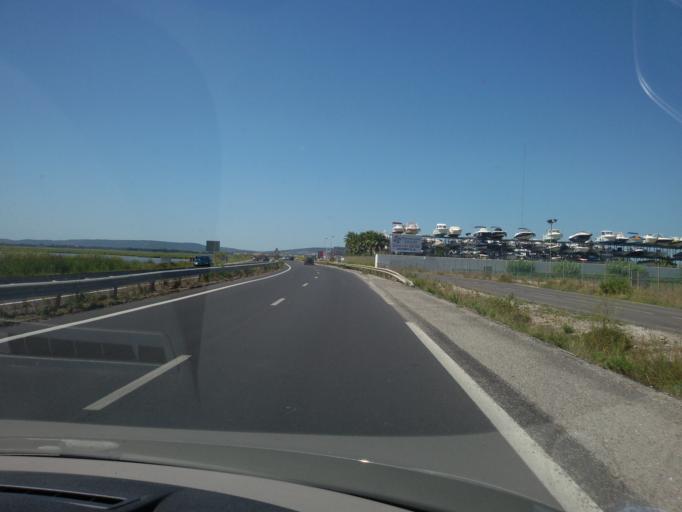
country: FR
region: Languedoc-Roussillon
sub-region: Departement de l'Herault
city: Palavas-les-Flots
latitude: 43.5348
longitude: 3.9120
